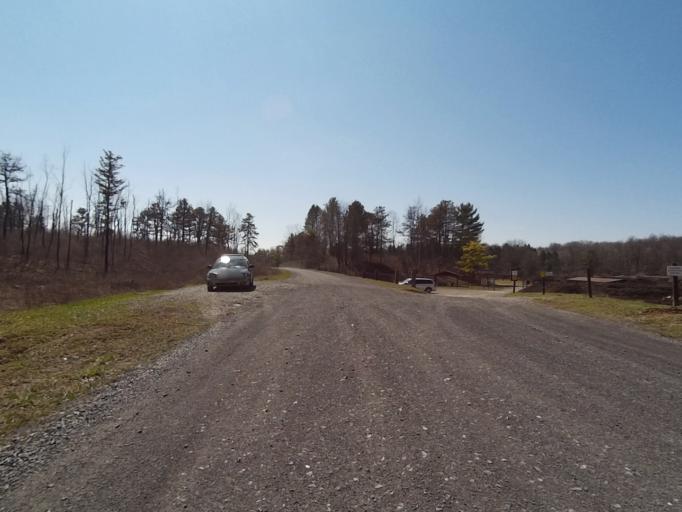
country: US
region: Pennsylvania
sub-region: Centre County
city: Stormstown
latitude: 40.7736
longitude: -77.9634
